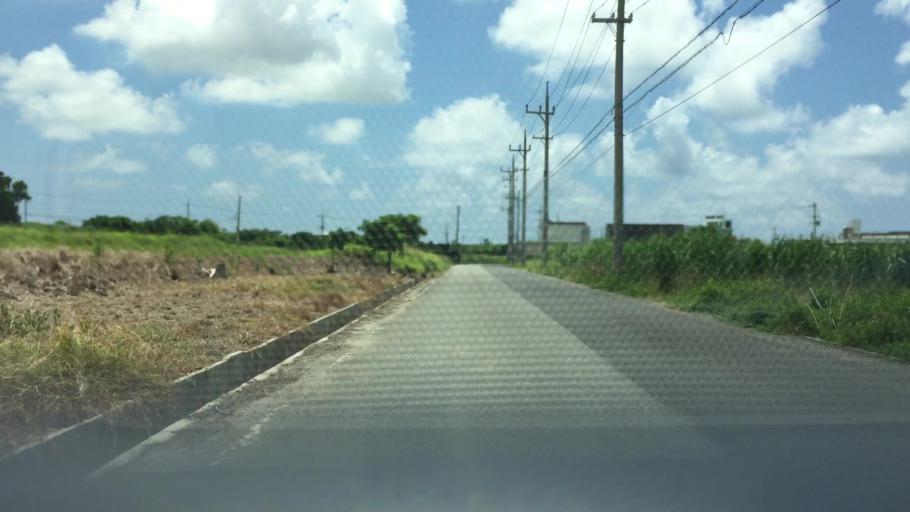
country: JP
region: Okinawa
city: Ishigaki
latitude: 24.3577
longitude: 124.1438
